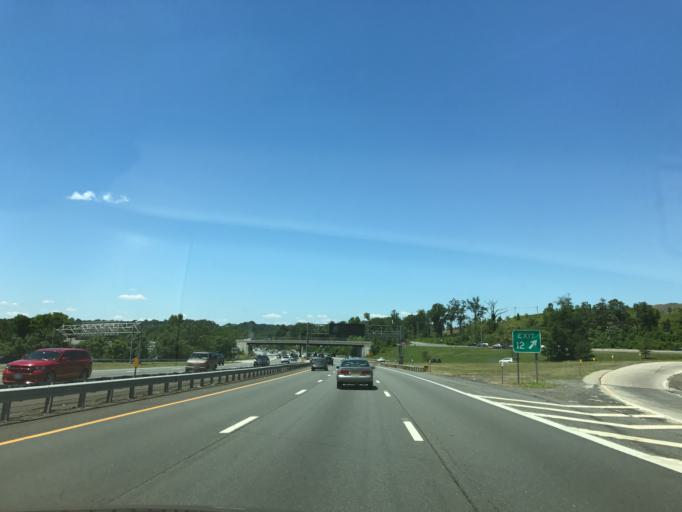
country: US
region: New York
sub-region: Rockland County
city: Valley Cottage
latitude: 41.1001
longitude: -73.9523
